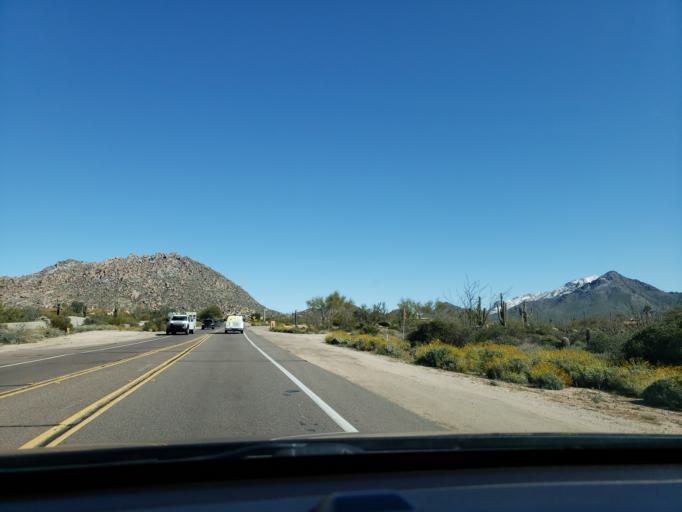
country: US
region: Arizona
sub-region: Maricopa County
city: Carefree
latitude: 33.7126
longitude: -111.8659
